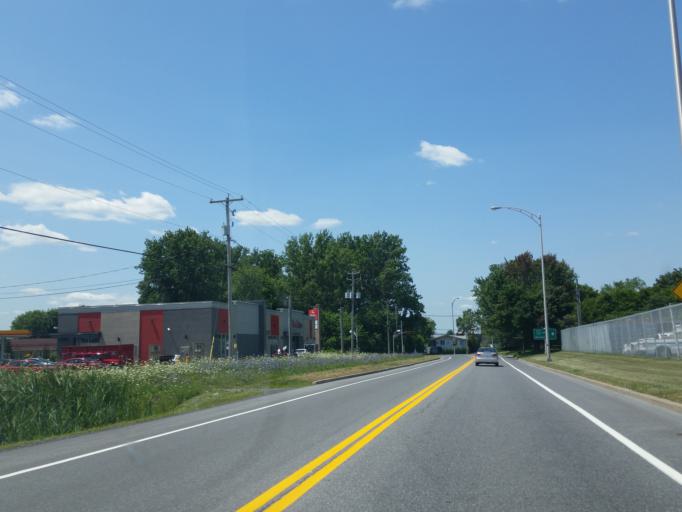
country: CA
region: Quebec
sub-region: Monteregie
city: Saint-Jean-sur-Richelieu
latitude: 45.3250
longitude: -73.2517
